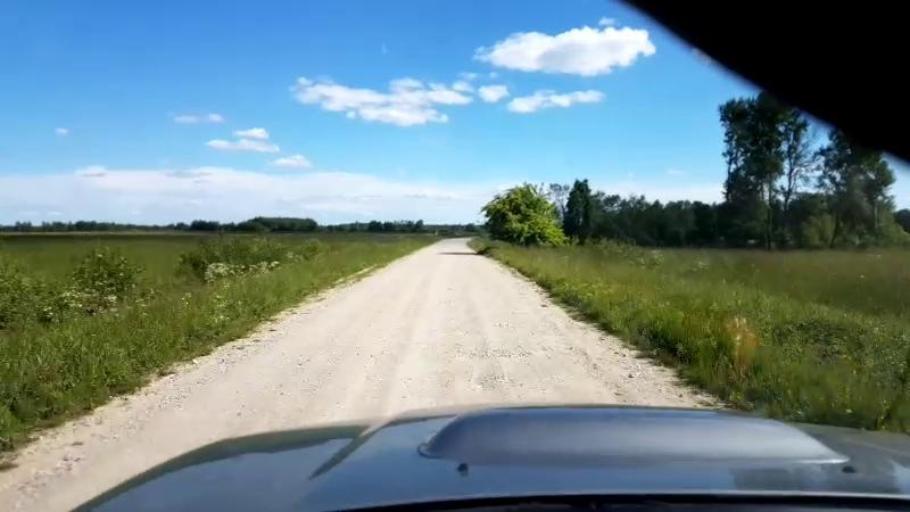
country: EE
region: Paernumaa
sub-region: Sauga vald
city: Sauga
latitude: 58.5044
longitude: 24.5219
